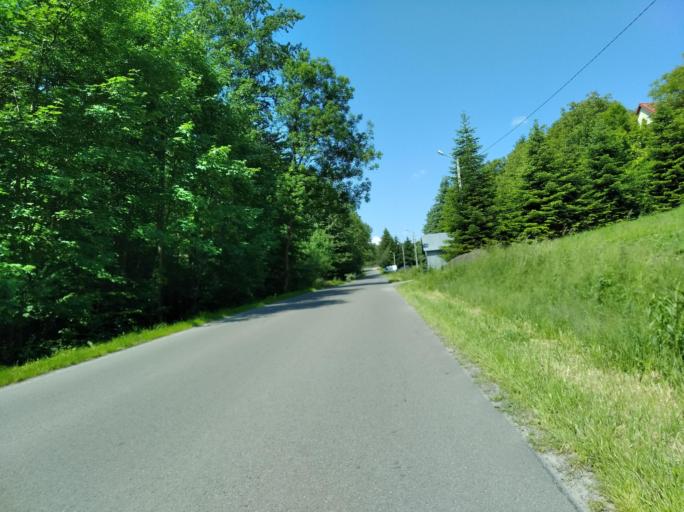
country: PL
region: Subcarpathian Voivodeship
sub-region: Powiat ropczycko-sedziszowski
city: Wielopole Skrzynskie
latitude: 49.9795
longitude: 21.6397
